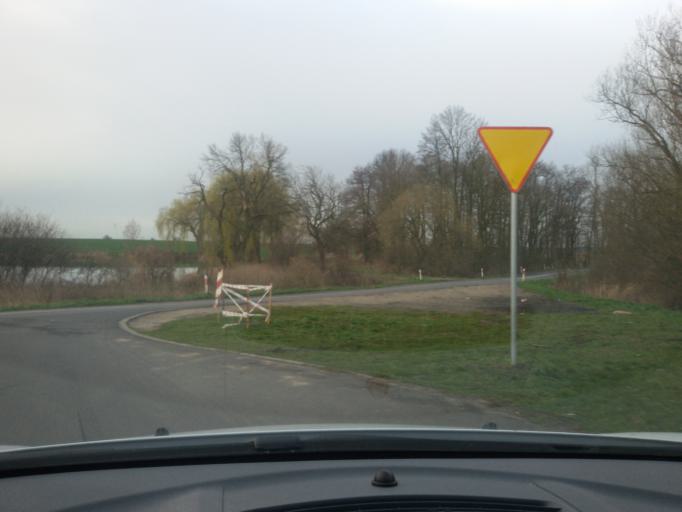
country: PL
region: Greater Poland Voivodeship
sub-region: Powiat gostynski
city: Krobia
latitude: 51.7653
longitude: 16.9267
